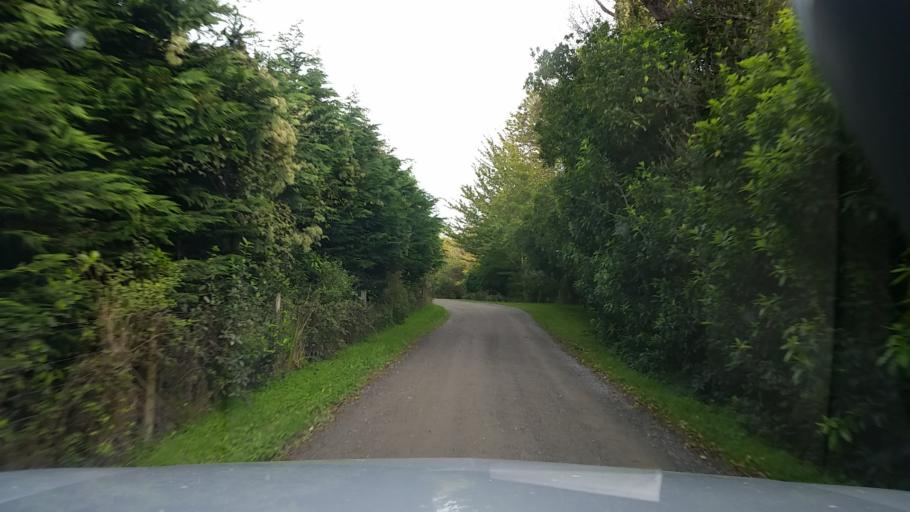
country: NZ
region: Marlborough
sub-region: Marlborough District
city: Blenheim
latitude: -41.4759
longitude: 173.9836
